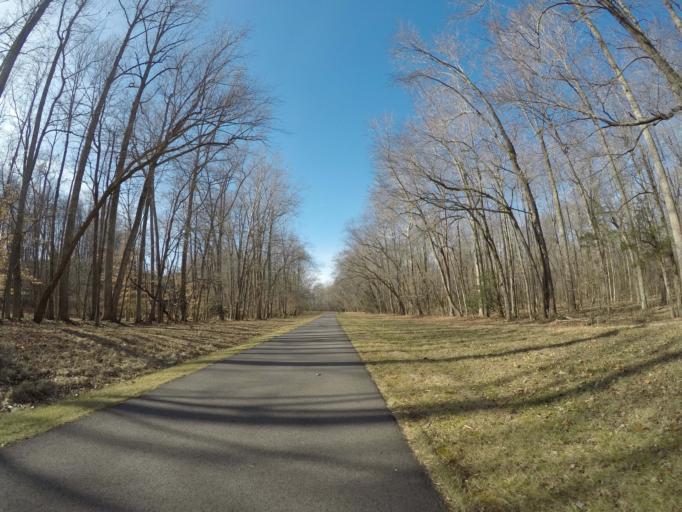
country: US
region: Maryland
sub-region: Charles County
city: Bennsville
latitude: 38.5963
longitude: -77.0334
